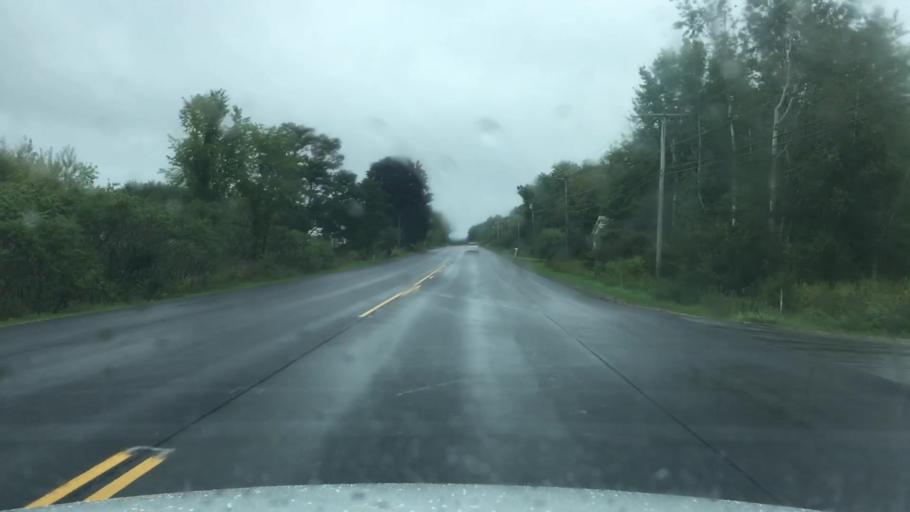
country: US
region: Maine
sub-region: Penobscot County
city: Hampden
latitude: 44.7607
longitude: -68.8476
